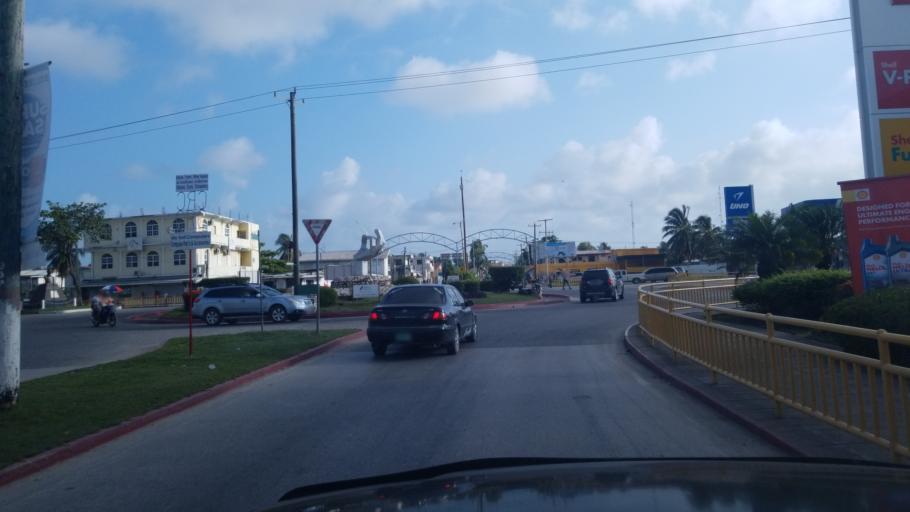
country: BZ
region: Belize
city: Belize City
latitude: 17.4950
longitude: -88.1989
